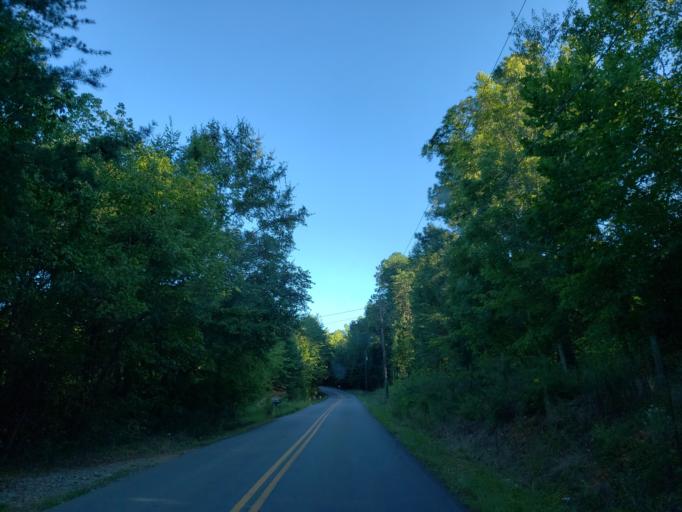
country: US
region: Georgia
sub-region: Bartow County
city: Rydal
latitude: 34.4158
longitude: -84.6932
